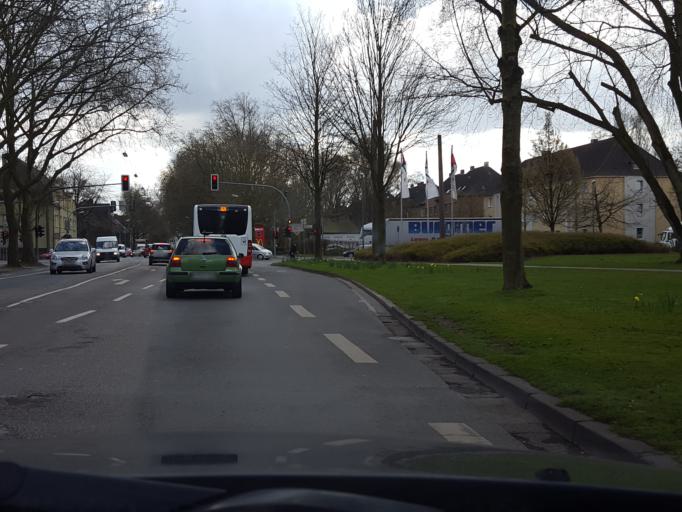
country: DE
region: North Rhine-Westphalia
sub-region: Regierungsbezirk Munster
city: Recklinghausen
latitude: 51.5941
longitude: 7.2073
